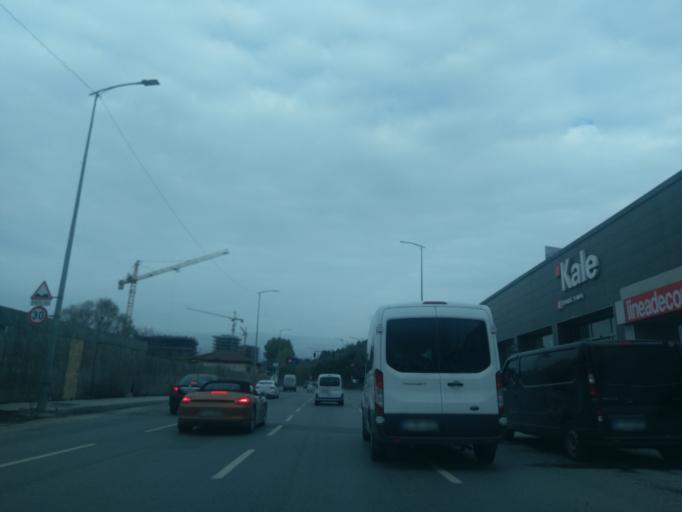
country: TR
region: Istanbul
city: Sisli
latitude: 41.0932
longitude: 28.9843
